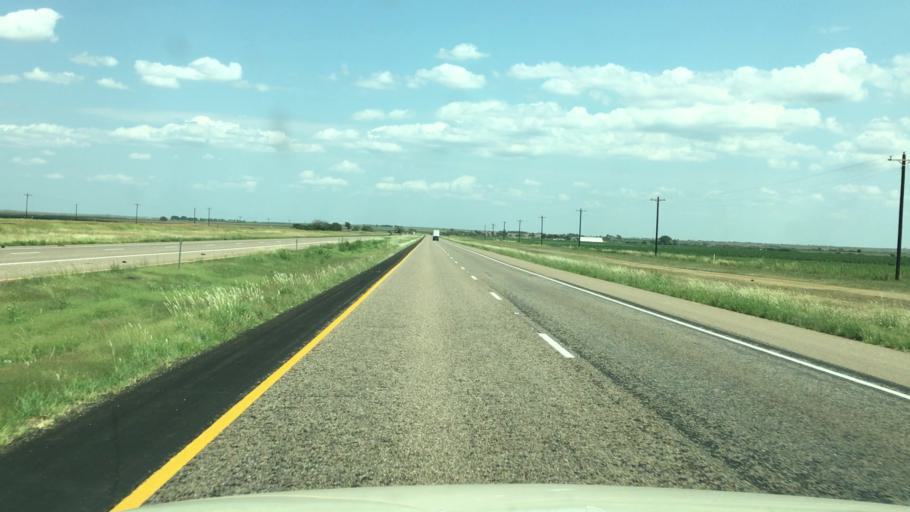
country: US
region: Texas
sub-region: Donley County
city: Clarendon
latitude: 35.0314
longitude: -101.1153
